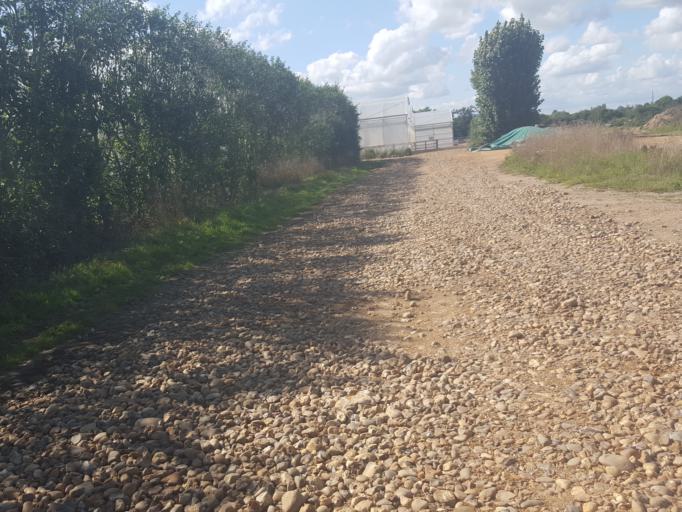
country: GB
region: England
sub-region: Essex
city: Alresford
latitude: 51.8550
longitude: 1.0208
